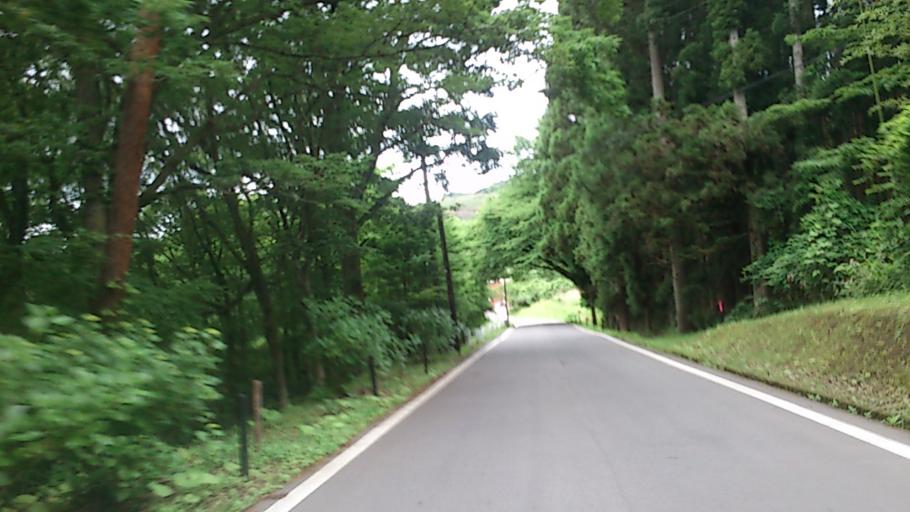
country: JP
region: Yamagata
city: Yuza
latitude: 39.1721
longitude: 139.9479
